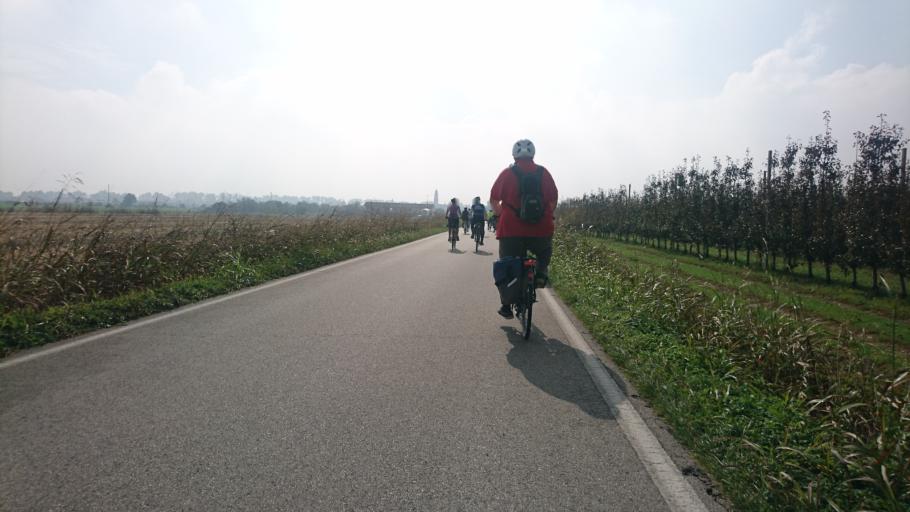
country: IT
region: Veneto
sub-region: Provincia di Padova
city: Boara Pisani
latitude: 45.1171
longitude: 11.7843
